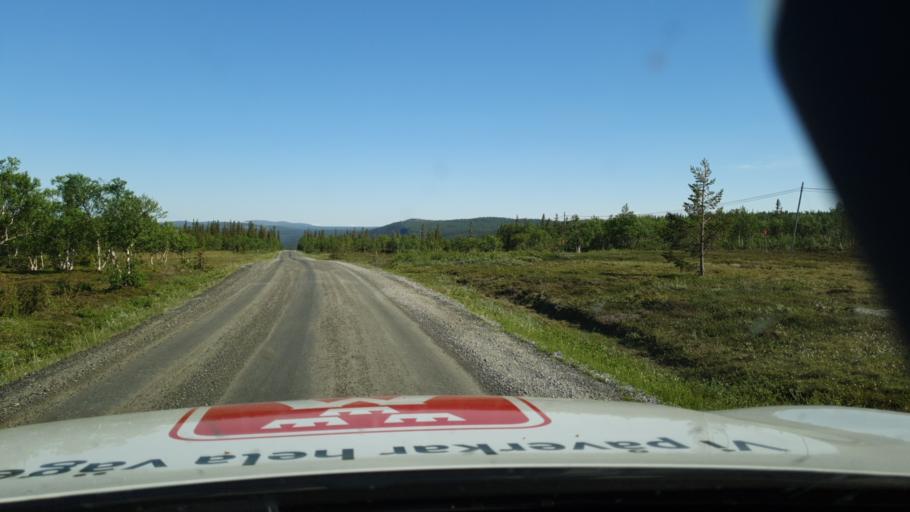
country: SE
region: Jaemtland
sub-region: Are Kommun
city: Are
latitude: 62.8757
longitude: 12.7356
